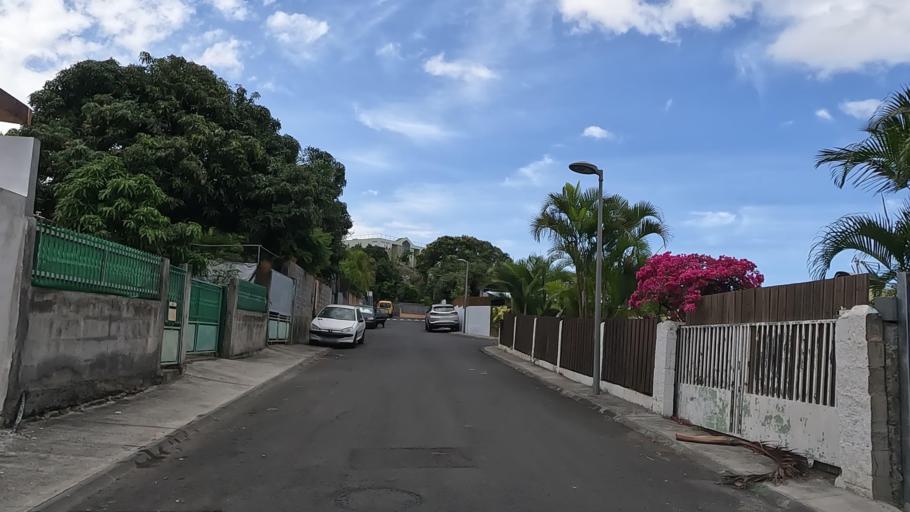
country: RE
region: Reunion
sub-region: Reunion
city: La Possession
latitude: -20.9483
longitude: 55.3305
